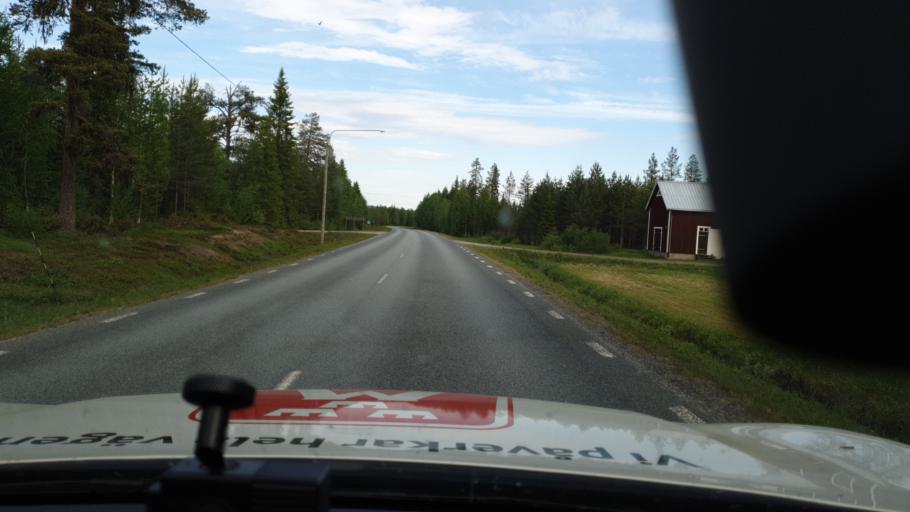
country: SE
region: Vaesterbotten
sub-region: Lycksele Kommun
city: Soderfors
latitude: 65.1262
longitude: 18.2805
